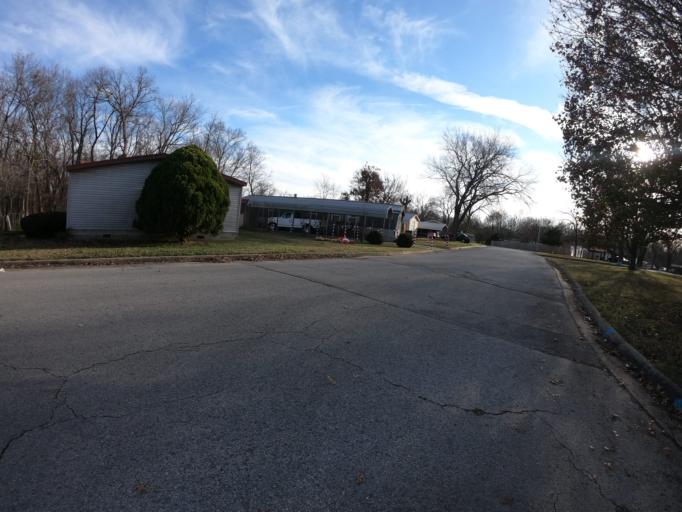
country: US
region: Arkansas
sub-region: Benton County
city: Rogers
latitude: 36.3332
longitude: -94.1699
